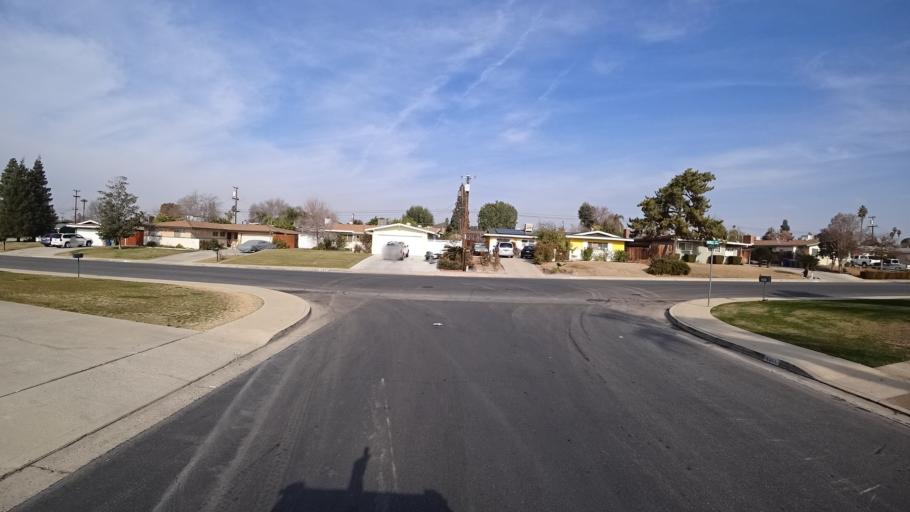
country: US
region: California
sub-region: Kern County
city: Oildale
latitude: 35.3997
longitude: -118.9617
